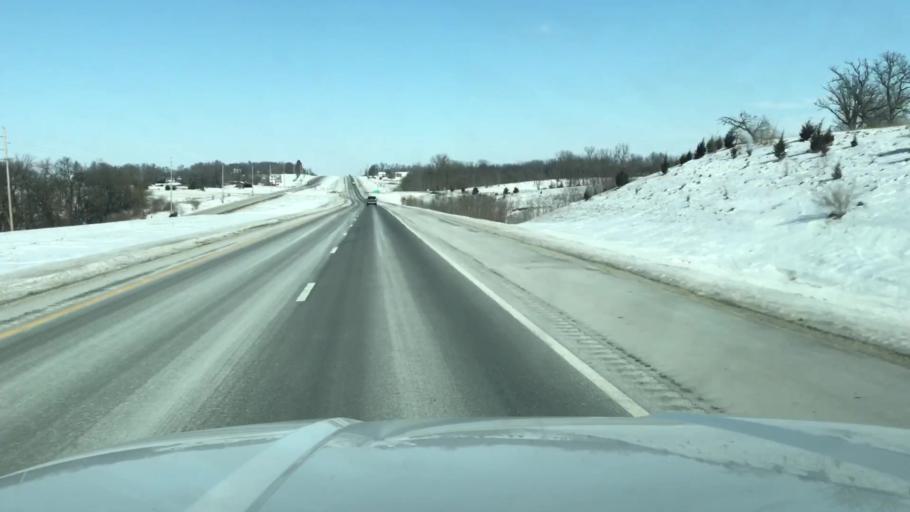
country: US
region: Missouri
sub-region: Nodaway County
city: Maryville
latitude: 40.1954
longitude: -94.8676
